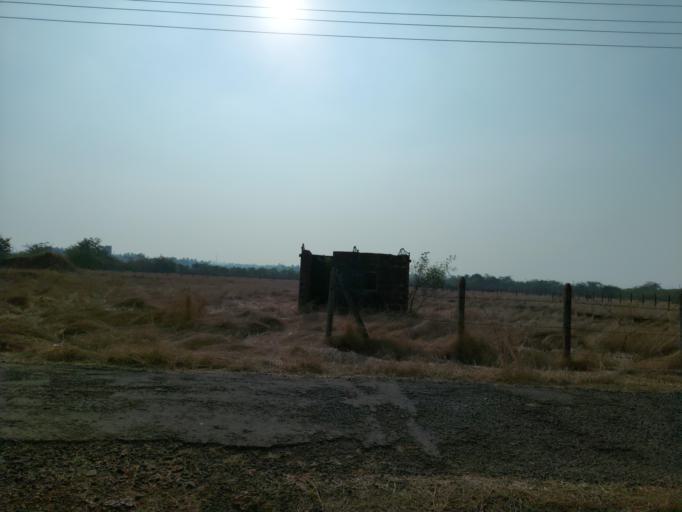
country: IN
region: Maharashtra
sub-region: Ratnagiri
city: Ratnagiri
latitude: 16.9369
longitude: 73.3239
